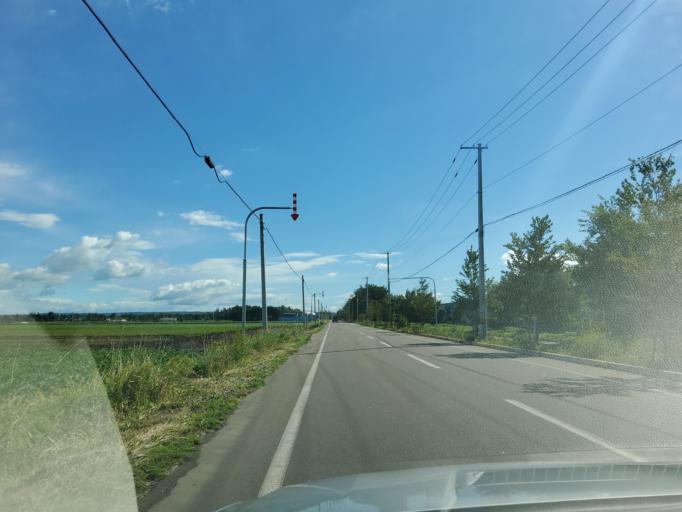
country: JP
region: Hokkaido
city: Otofuke
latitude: 42.9904
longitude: 143.1761
